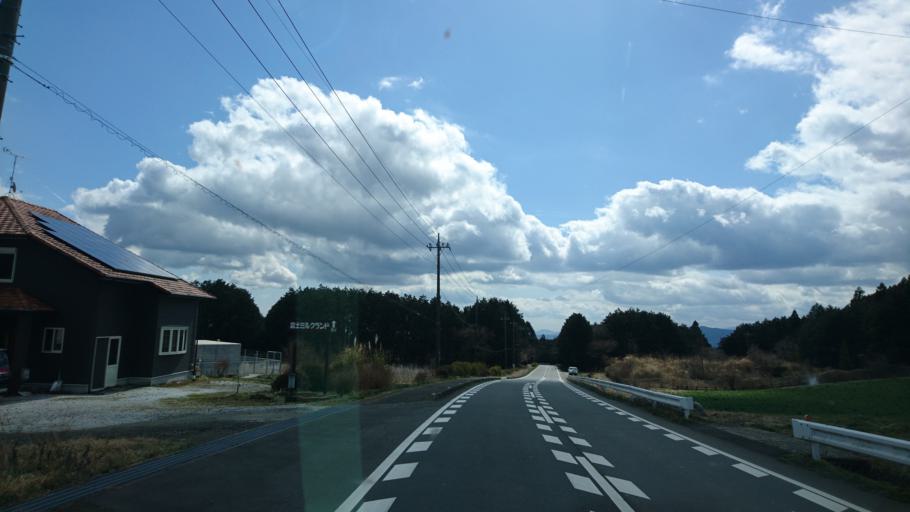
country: JP
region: Yamanashi
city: Fujikawaguchiko
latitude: 35.3744
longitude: 138.6025
